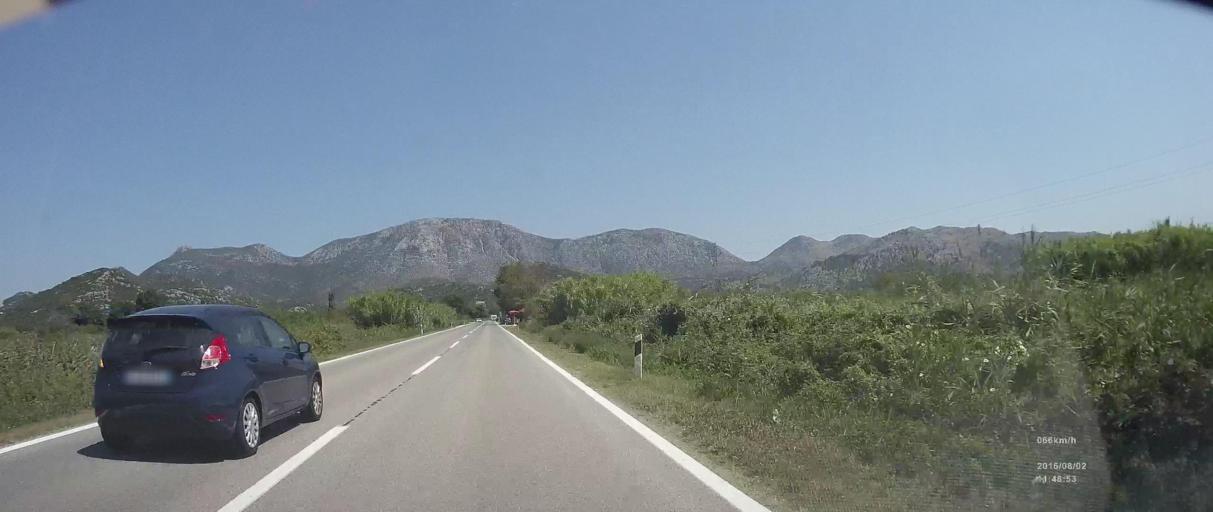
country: HR
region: Dubrovacko-Neretvanska
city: Komin
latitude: 43.0380
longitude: 17.4932
